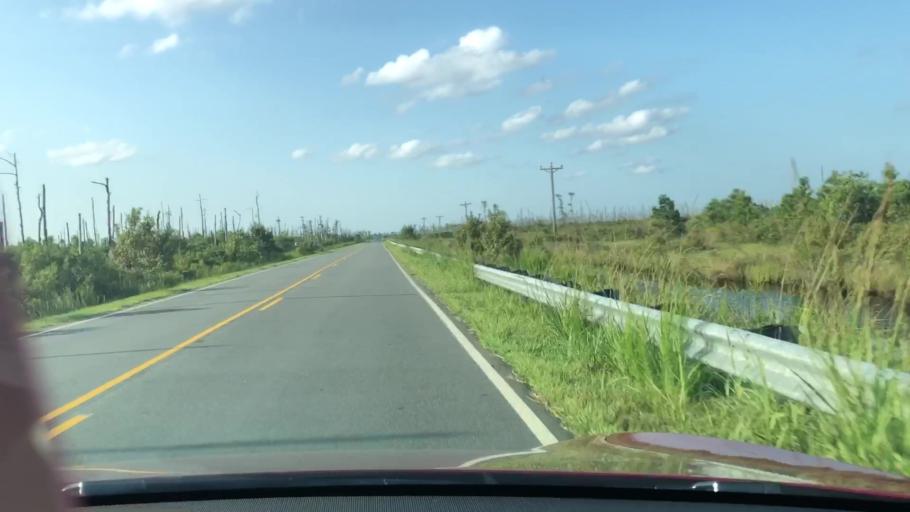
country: US
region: North Carolina
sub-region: Dare County
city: Wanchese
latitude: 35.6447
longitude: -75.7770
